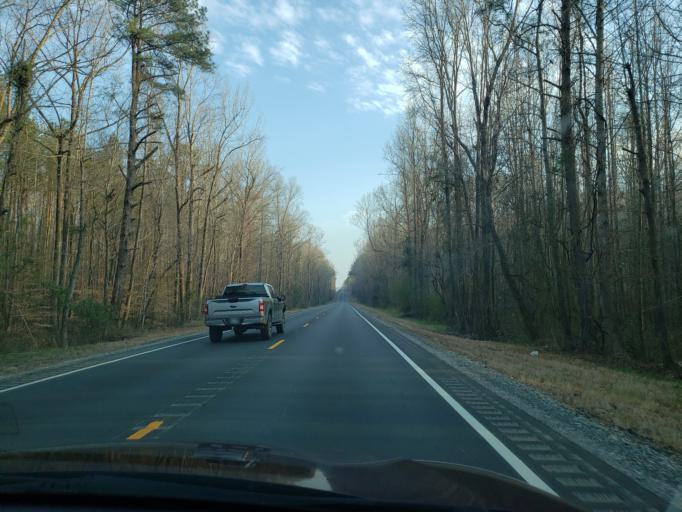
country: US
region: Alabama
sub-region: Hale County
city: Greensboro
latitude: 32.8457
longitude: -87.6101
